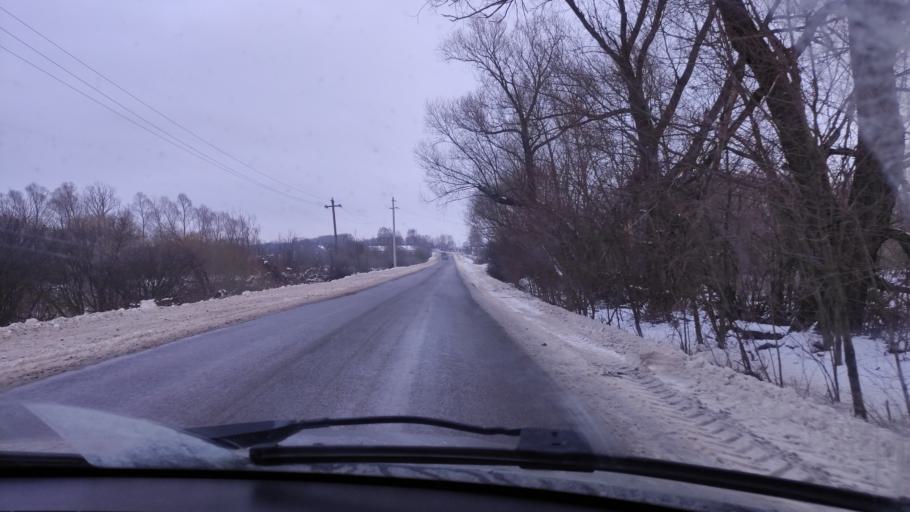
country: RU
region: Tambov
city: Pervomayskiy
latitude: 53.3024
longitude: 40.3715
